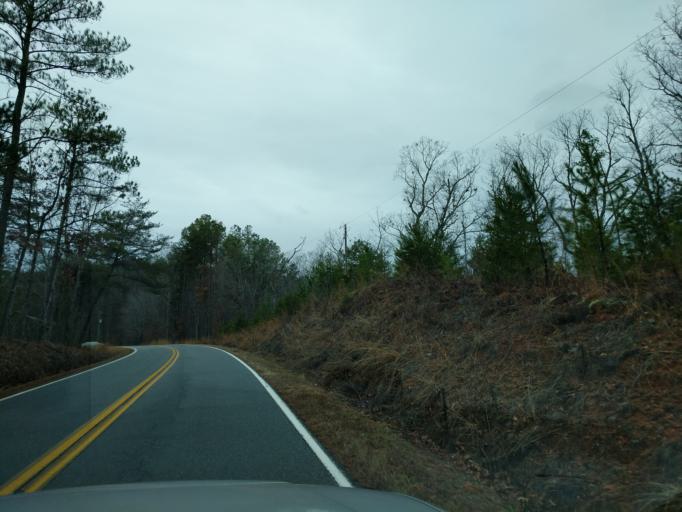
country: US
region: South Carolina
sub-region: Oconee County
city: Walhalla
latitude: 34.7952
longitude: -83.2219
